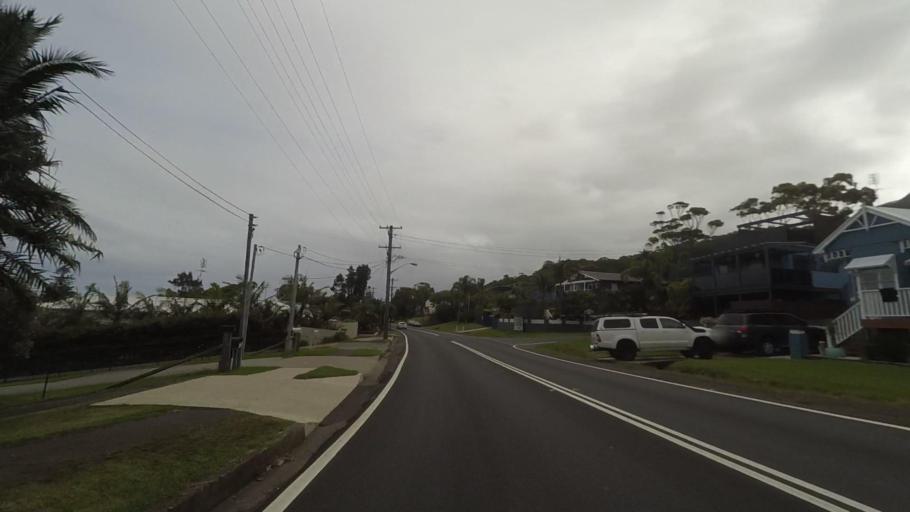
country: AU
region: New South Wales
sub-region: Wollongong
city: Bulli
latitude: -34.2772
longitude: 150.9546
